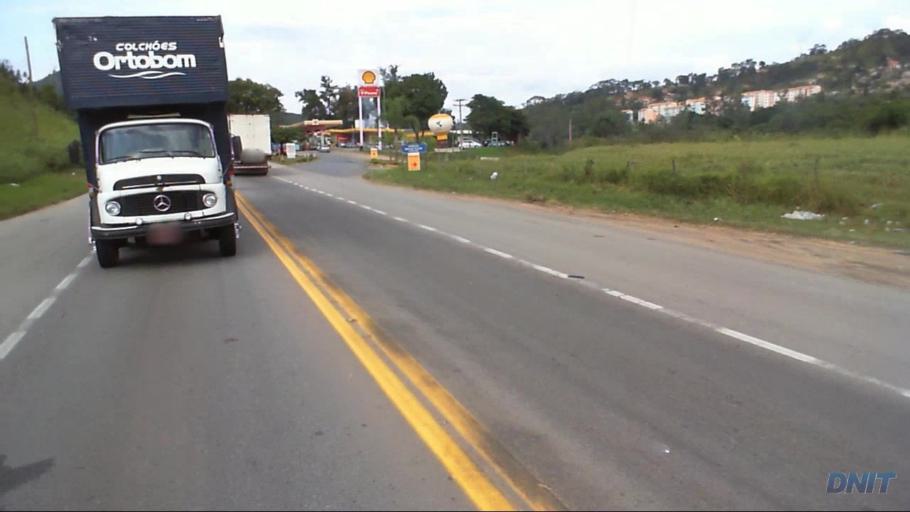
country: BR
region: Minas Gerais
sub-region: Santa Luzia
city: Santa Luzia
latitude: -19.8396
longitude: -43.8776
